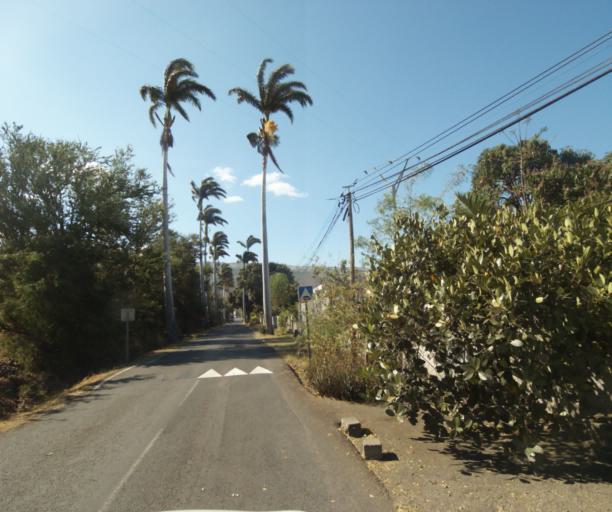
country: RE
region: Reunion
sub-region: Reunion
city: Saint-Paul
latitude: -20.9837
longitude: 55.2956
